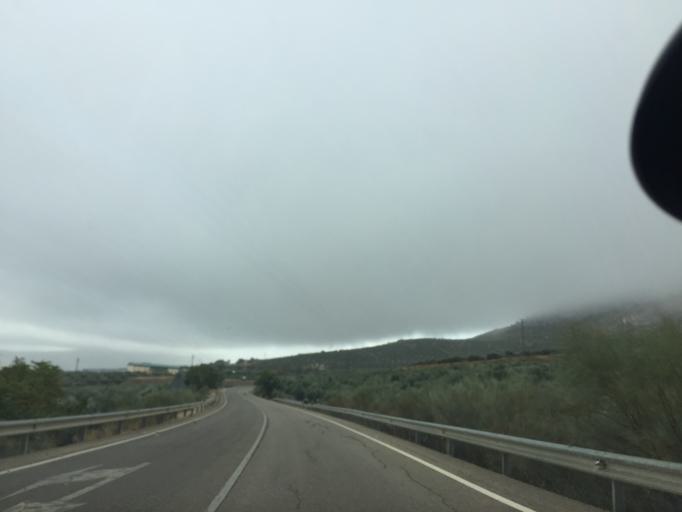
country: ES
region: Andalusia
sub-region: Provincia de Jaen
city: Jimena
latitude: 37.8466
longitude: -3.4985
